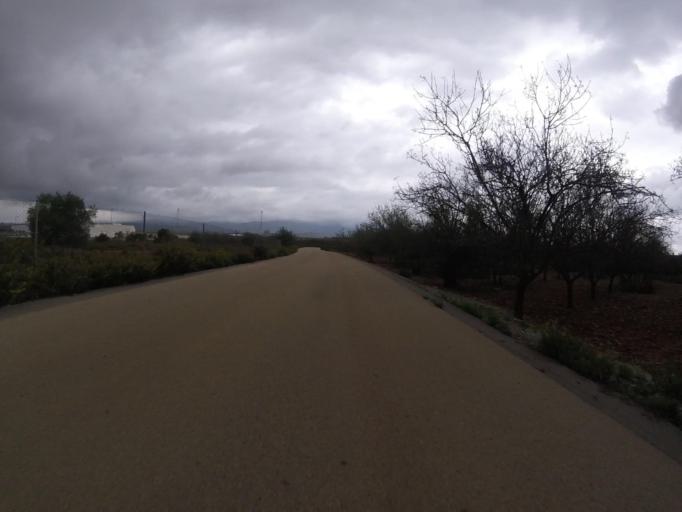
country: ES
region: Valencia
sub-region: Provincia de Castello
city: Benlloch
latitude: 40.2048
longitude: 0.0718
